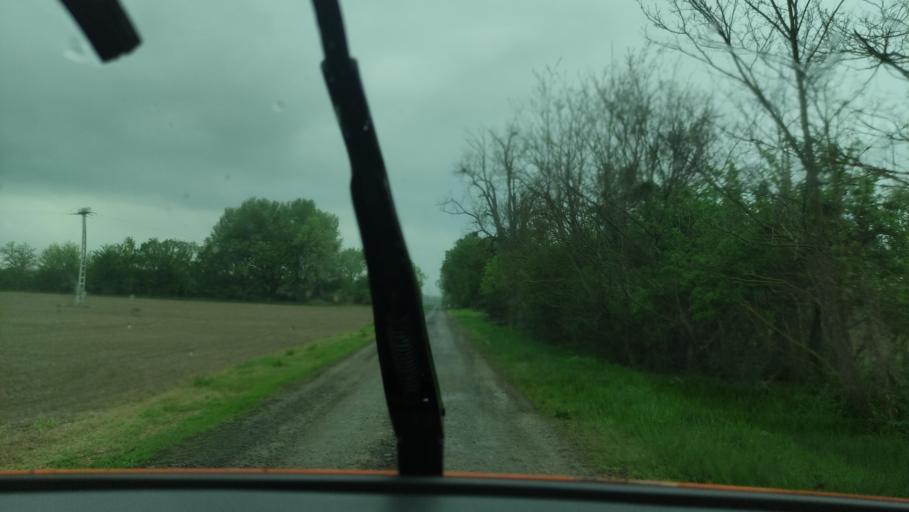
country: HR
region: Osjecko-Baranjska
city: Batina
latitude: 45.8981
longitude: 18.7831
